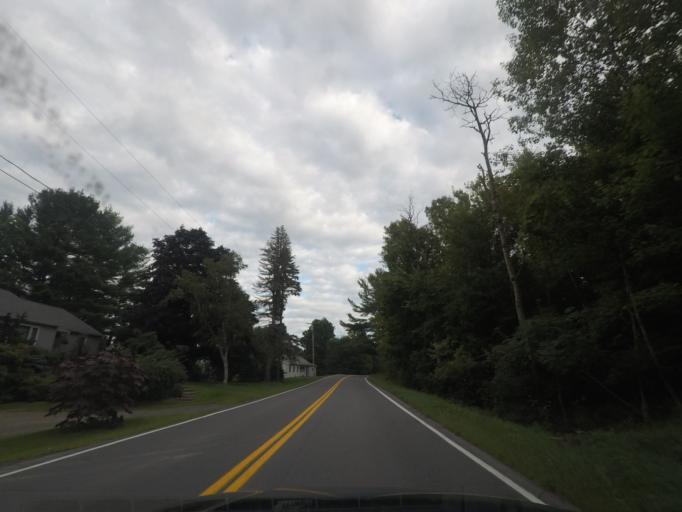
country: US
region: New York
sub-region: Rensselaer County
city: Nassau
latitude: 42.5450
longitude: -73.6096
